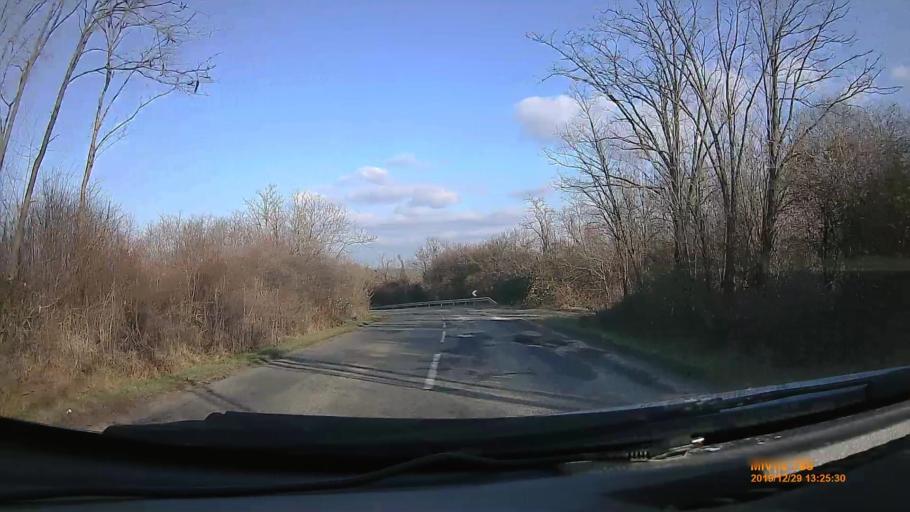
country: HU
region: Heves
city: Verpelet
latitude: 47.8484
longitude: 20.1964
